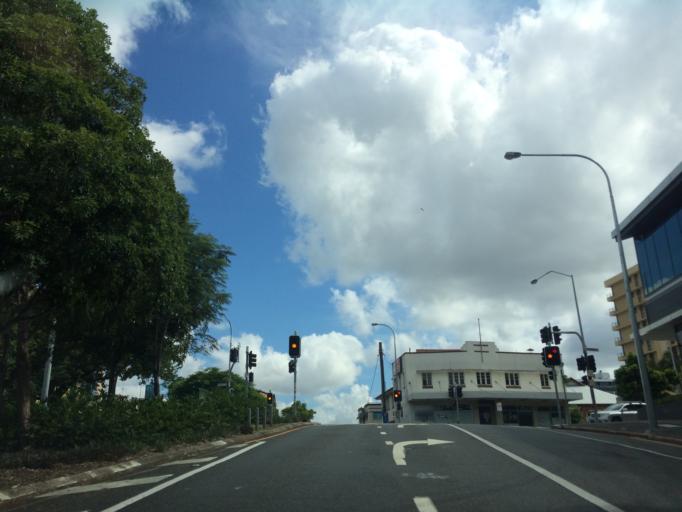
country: AU
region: Queensland
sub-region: Brisbane
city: Spring Hill
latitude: -27.4625
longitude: 153.0212
